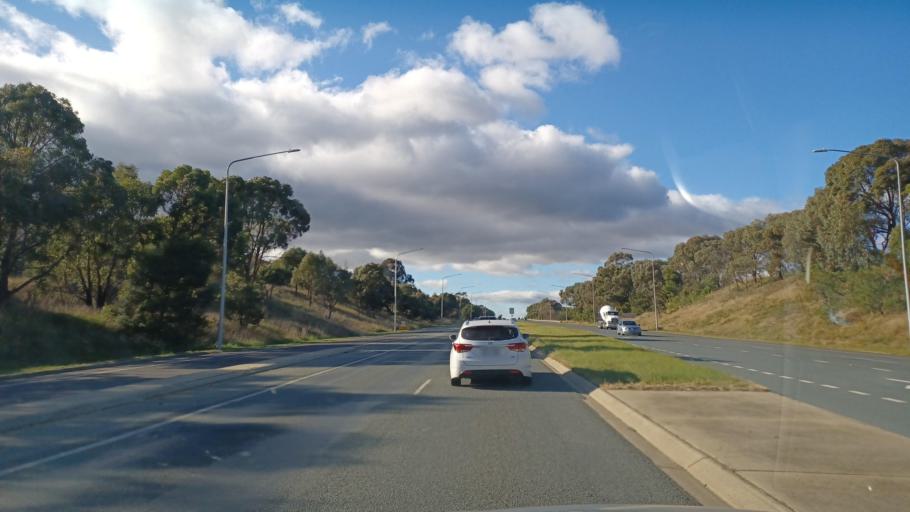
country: AU
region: Australian Capital Territory
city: Macquarie
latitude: -35.2702
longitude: 149.0540
